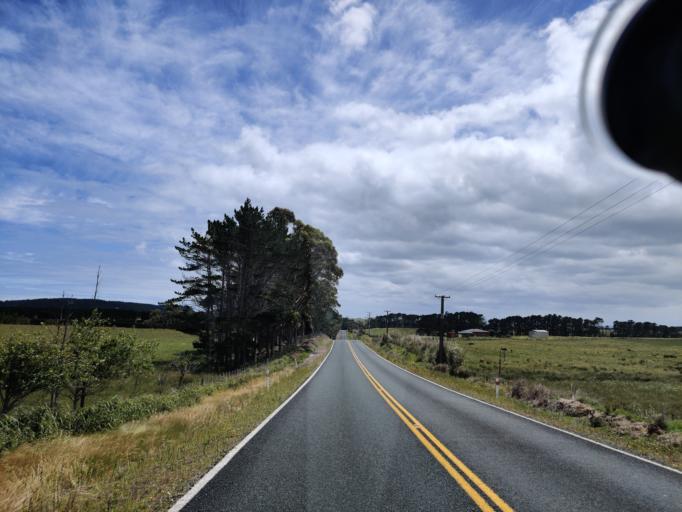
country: NZ
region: Northland
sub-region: Far North District
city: Kaitaia
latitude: -34.7168
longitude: 173.0396
